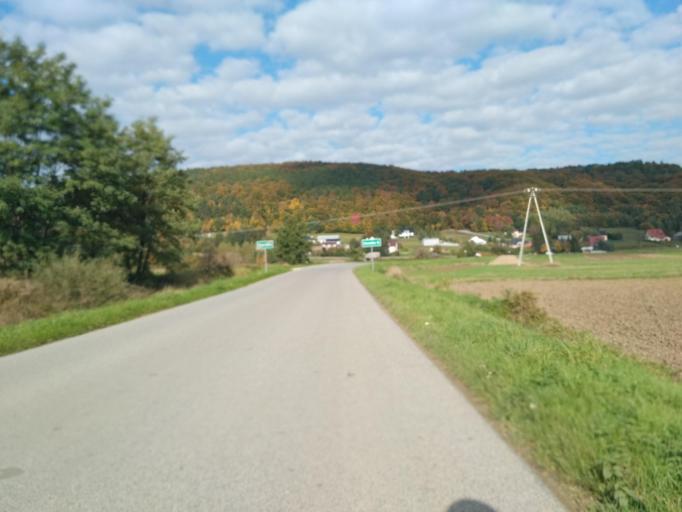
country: PL
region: Subcarpathian Voivodeship
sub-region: Powiat debicki
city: Brzostek
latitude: 49.8957
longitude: 21.3721
